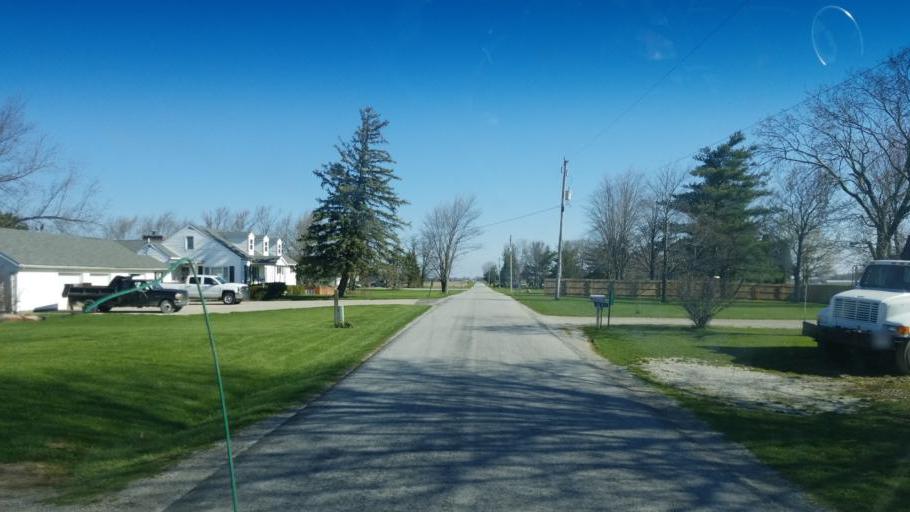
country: US
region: Ohio
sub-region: Hardin County
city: Kenton
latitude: 40.6636
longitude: -83.5622
